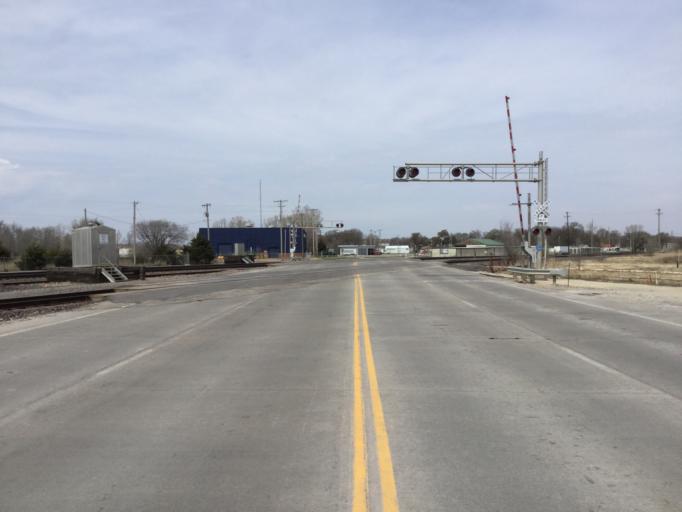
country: US
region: Kansas
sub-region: Butler County
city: Augusta
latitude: 37.6694
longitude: -96.9811
